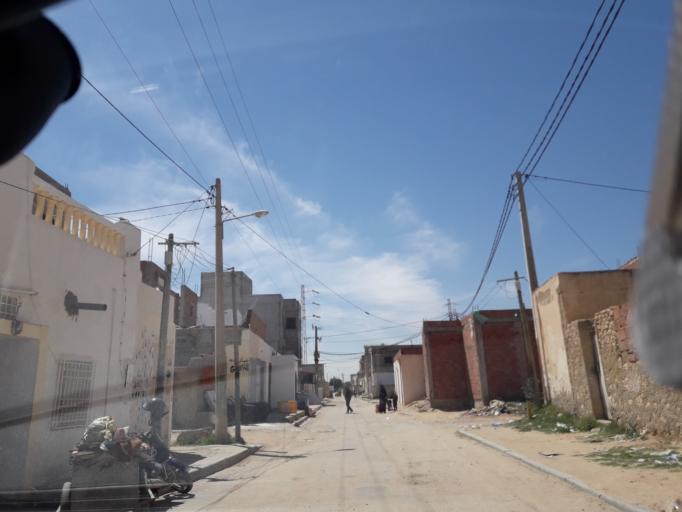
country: TN
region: Safaqis
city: Sfax
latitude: 34.7384
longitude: 10.5242
